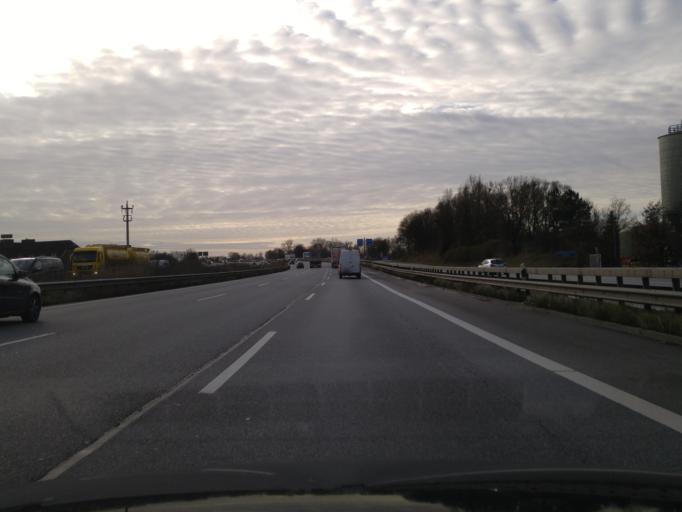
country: DE
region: Hamburg
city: Harburg
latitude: 53.4830
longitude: 10.0249
